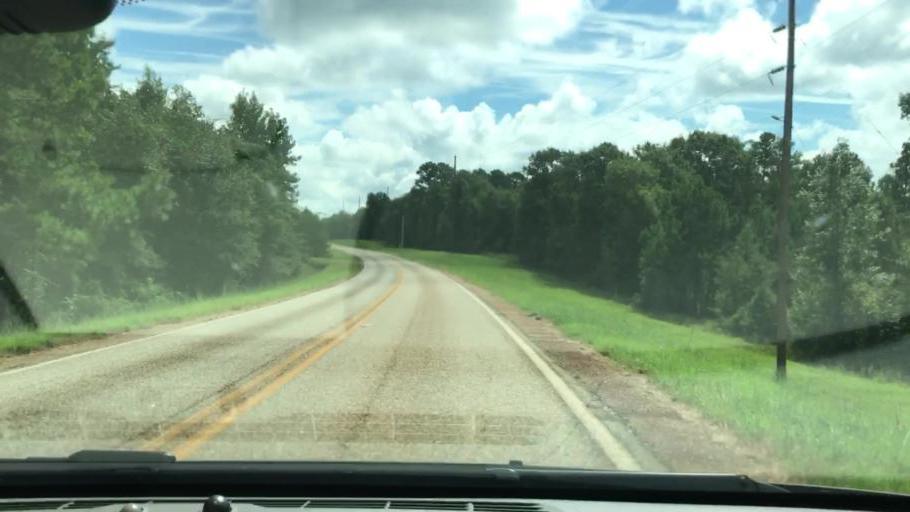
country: US
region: Georgia
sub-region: Stewart County
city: Lumpkin
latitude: 32.0633
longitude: -84.8351
